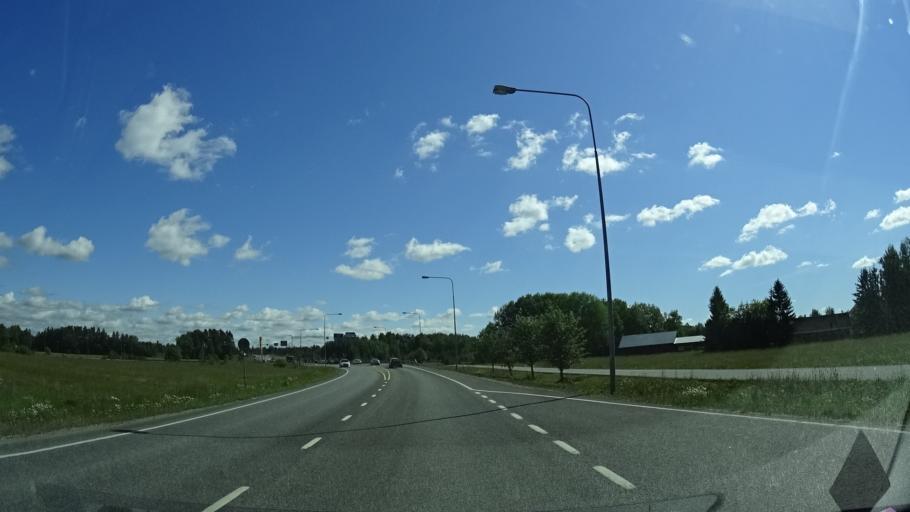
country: FI
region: Varsinais-Suomi
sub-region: Turku
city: Raisio
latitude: 60.5040
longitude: 22.1475
